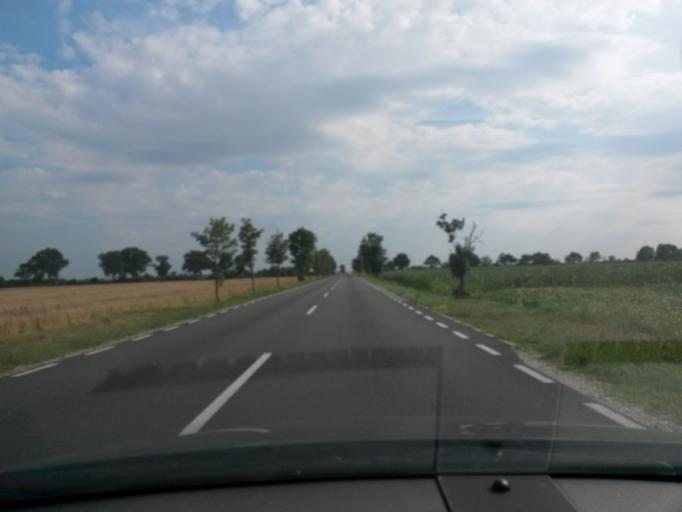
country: PL
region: Greater Poland Voivodeship
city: Miejska Gorka
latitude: 51.7184
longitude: 16.9475
